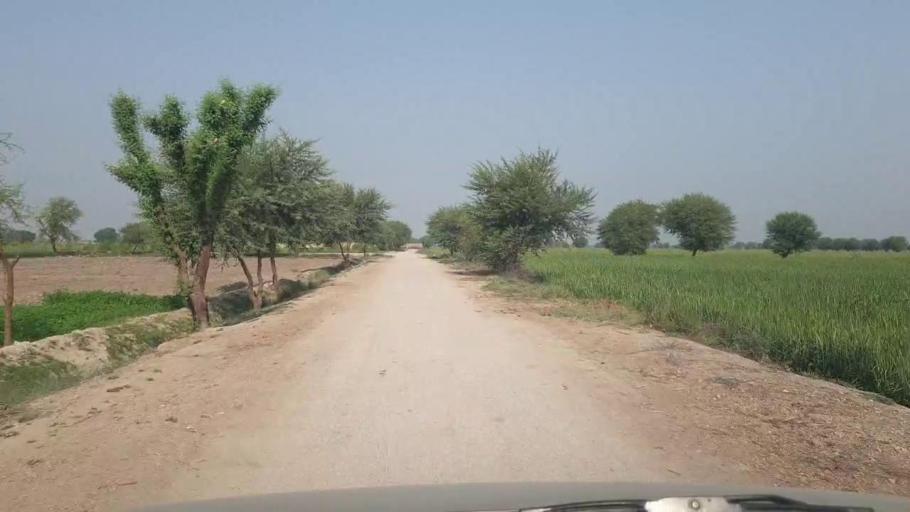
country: PK
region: Sindh
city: Umarkot
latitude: 25.4058
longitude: 69.7196
